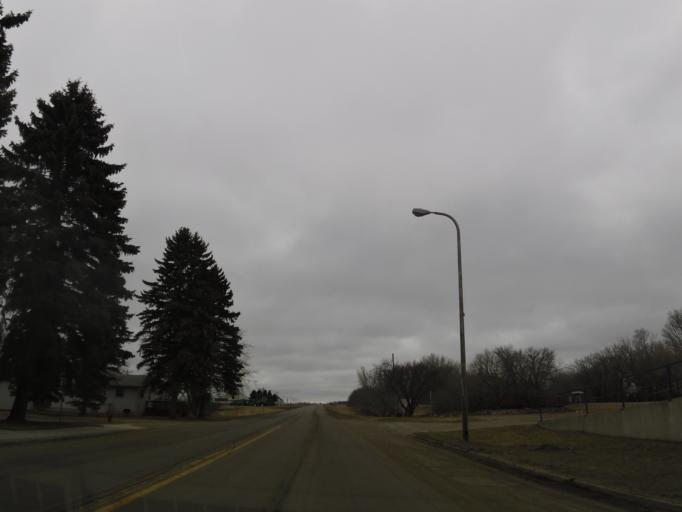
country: US
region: North Dakota
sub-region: Traill County
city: Hillsboro
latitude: 47.1890
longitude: -97.2175
